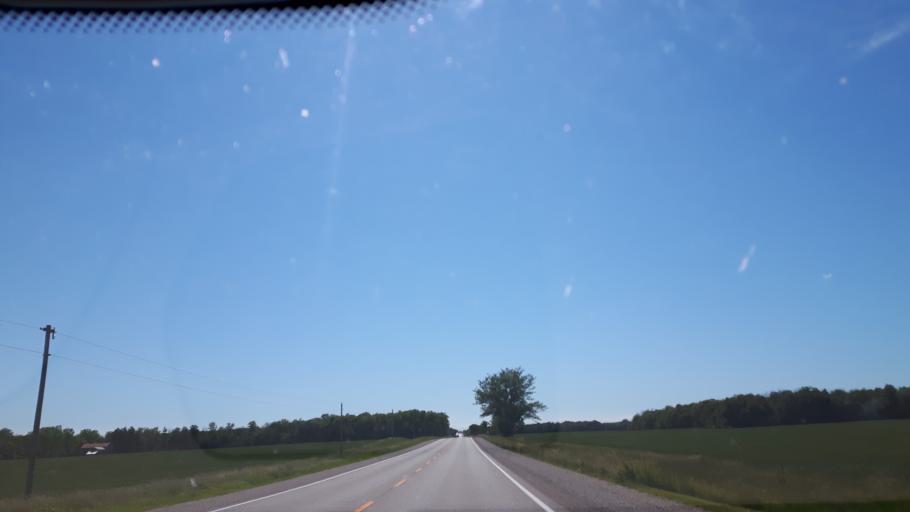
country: CA
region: Ontario
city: Bluewater
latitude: 43.4318
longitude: -81.5244
